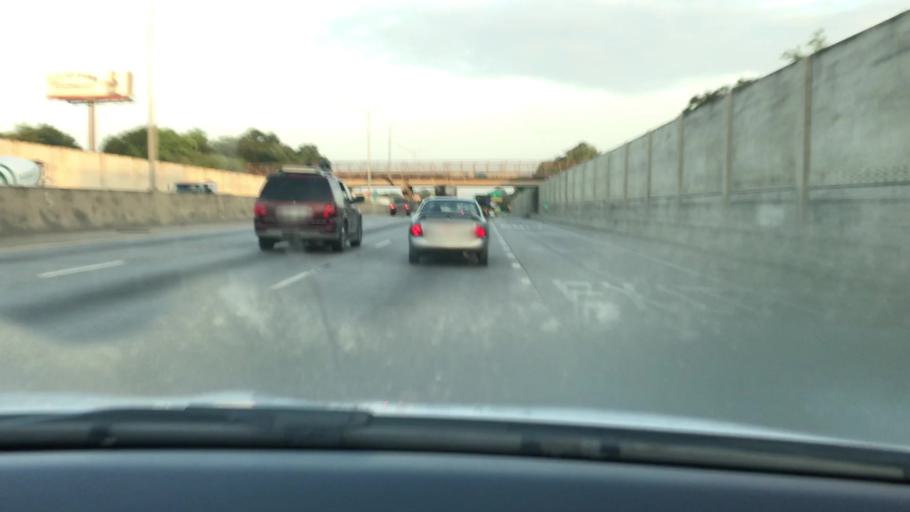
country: US
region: Louisiana
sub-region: East Baton Rouge Parish
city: Baton Rouge
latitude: 30.4236
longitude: -91.1443
